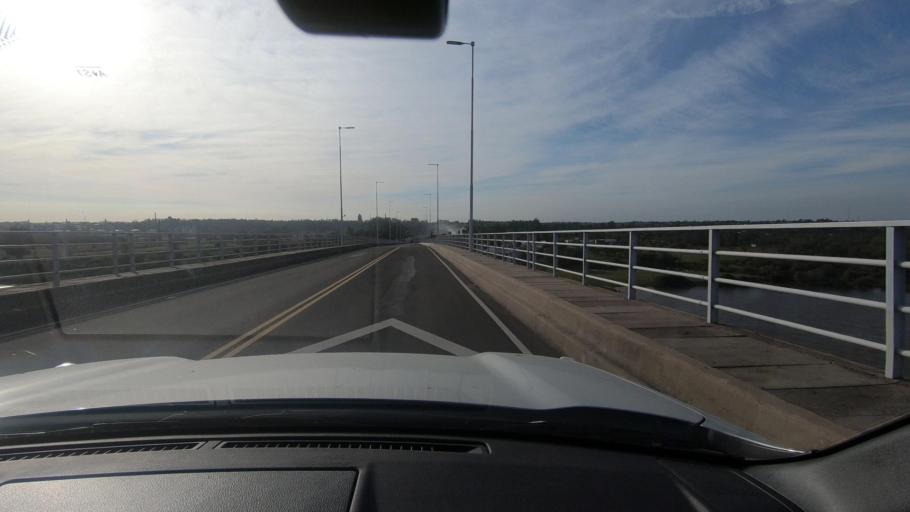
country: AR
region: Entre Rios
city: Colon
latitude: -32.2415
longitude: -58.1526
